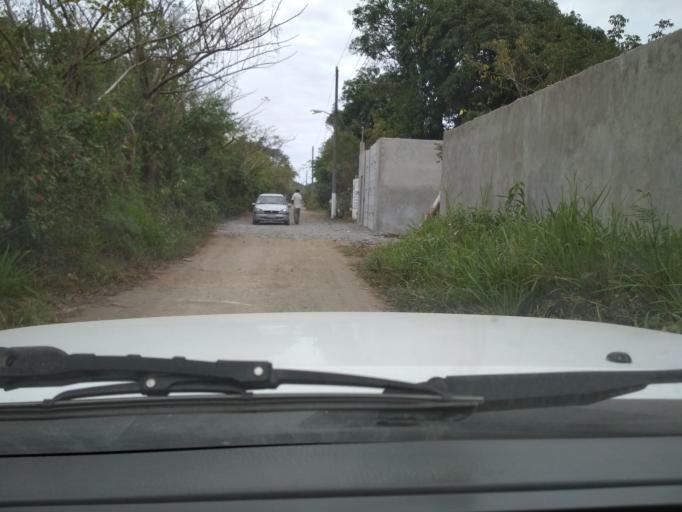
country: MX
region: Veracruz
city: El Tejar
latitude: 19.0708
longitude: -96.1428
